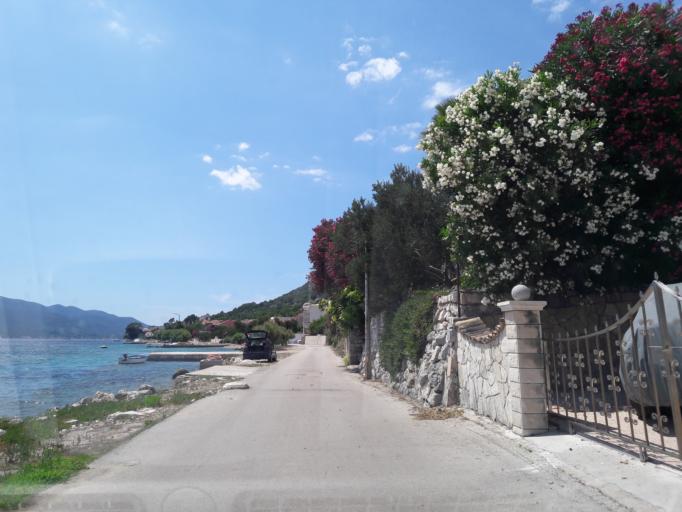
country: HR
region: Dubrovacko-Neretvanska
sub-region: Grad Korcula
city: Zrnovo
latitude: 42.9849
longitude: 17.0956
